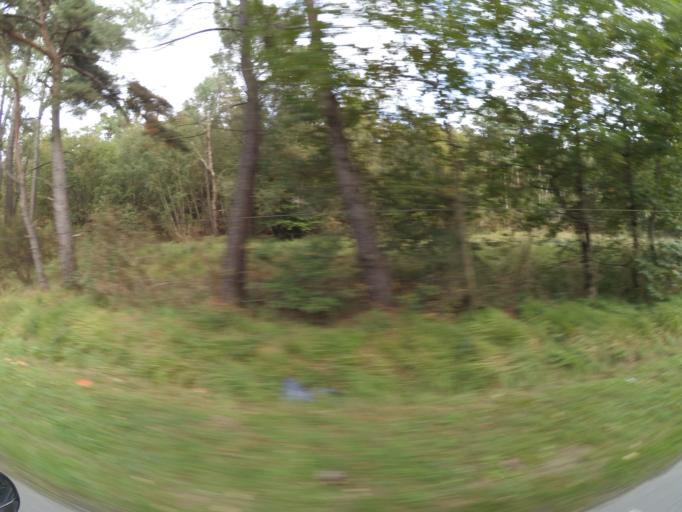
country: FR
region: Pays de la Loire
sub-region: Departement de la Loire-Atlantique
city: Plesse
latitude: 47.5022
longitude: -1.8700
